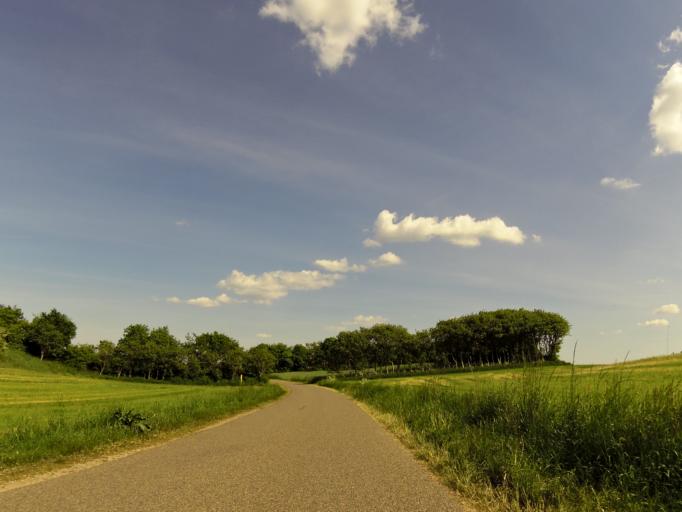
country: DK
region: Central Jutland
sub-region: Holstebro Kommune
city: Vinderup
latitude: 56.4343
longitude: 8.8829
